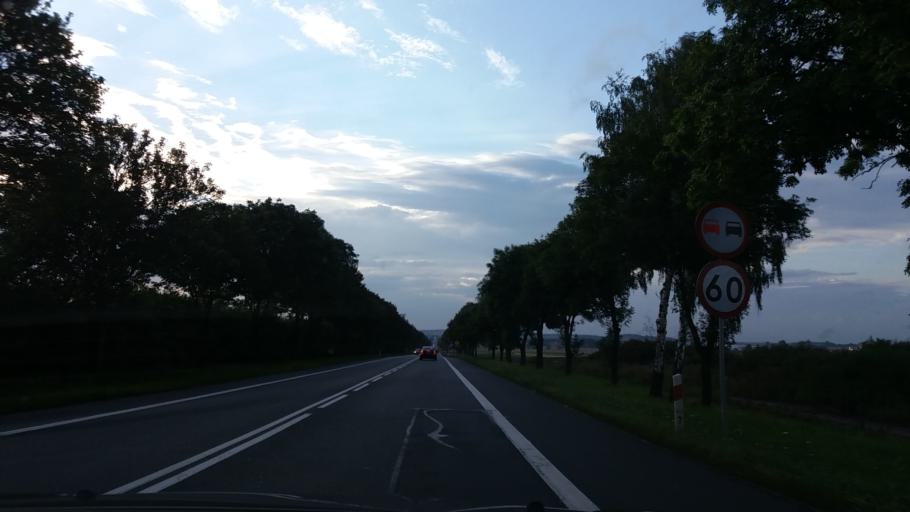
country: PL
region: Lower Silesian Voivodeship
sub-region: Powiat polkowicki
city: Radwanice
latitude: 51.6047
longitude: 15.9514
